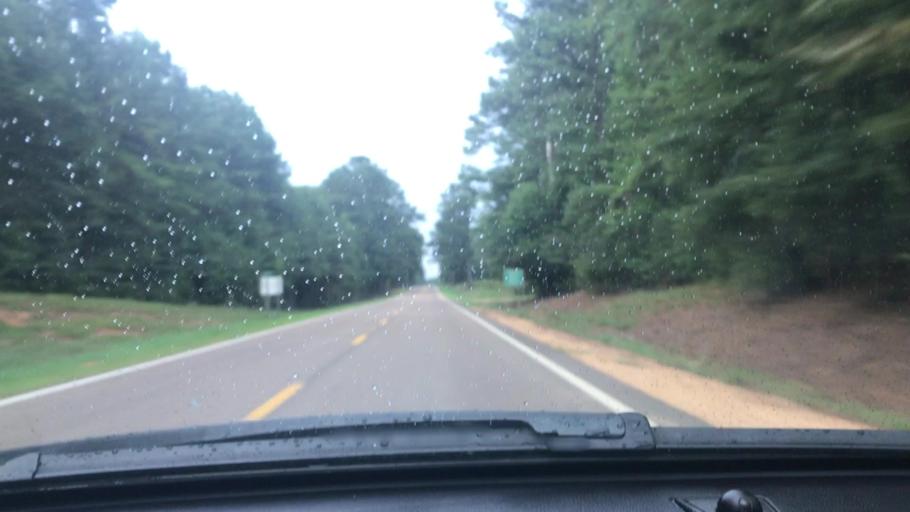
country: US
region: Mississippi
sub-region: Pike County
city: Summit
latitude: 31.3495
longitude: -90.5995
